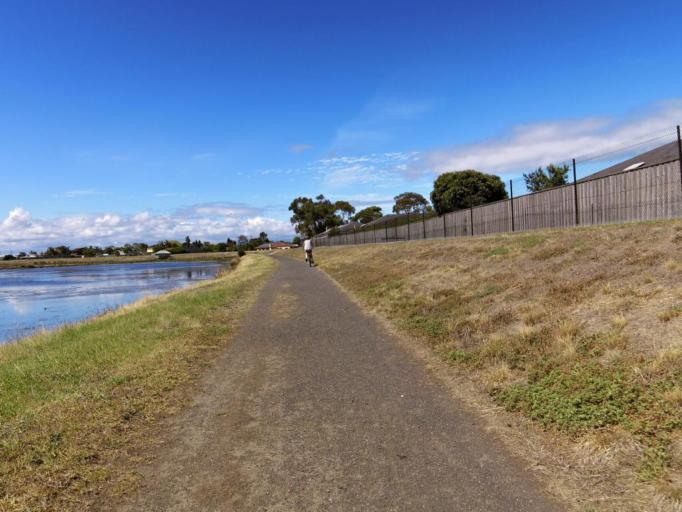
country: AU
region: Victoria
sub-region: Hobsons Bay
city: Altona Meadows
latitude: -37.8707
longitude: 144.8035
